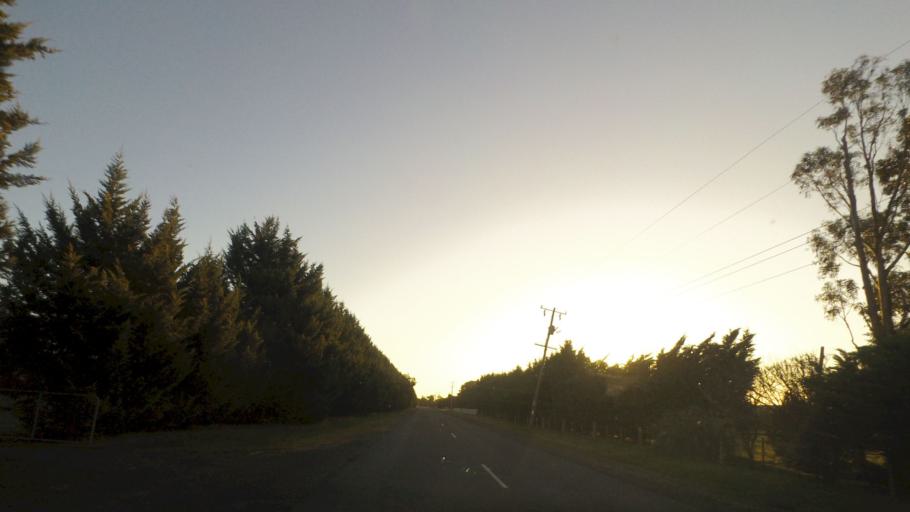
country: AU
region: Victoria
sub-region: Hume
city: Sunbury
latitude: -37.5036
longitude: 144.6176
